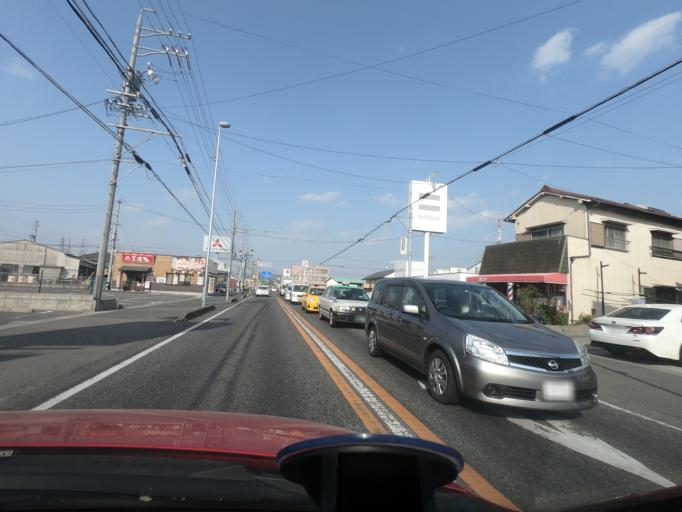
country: JP
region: Aichi
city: Kasugai
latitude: 35.2582
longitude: 136.9948
